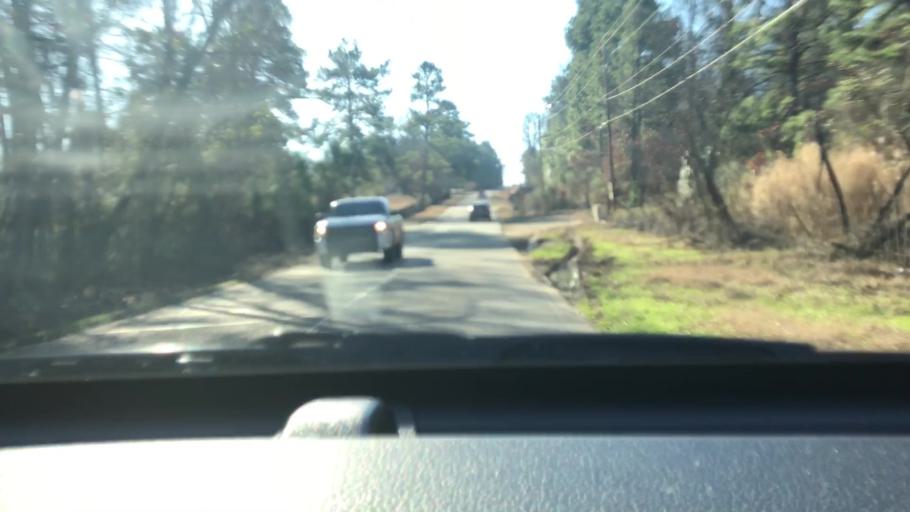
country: US
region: Arkansas
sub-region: Hempstead County
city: Hope
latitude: 33.6396
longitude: -93.5837
